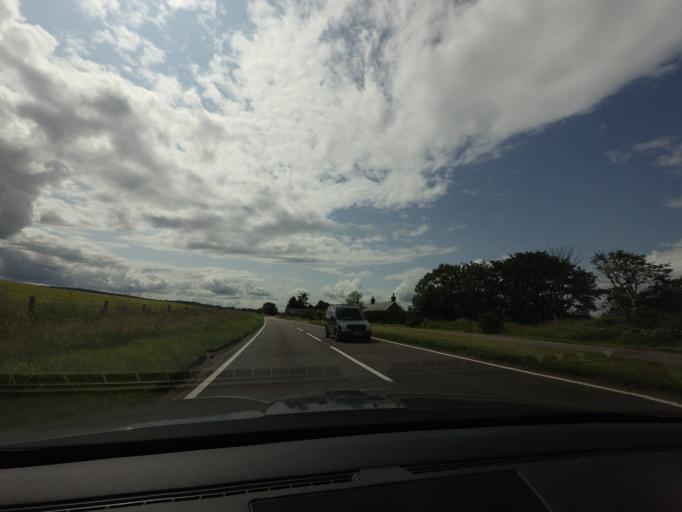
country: GB
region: Scotland
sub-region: Moray
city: Kinloss
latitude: 57.6323
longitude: -3.5019
